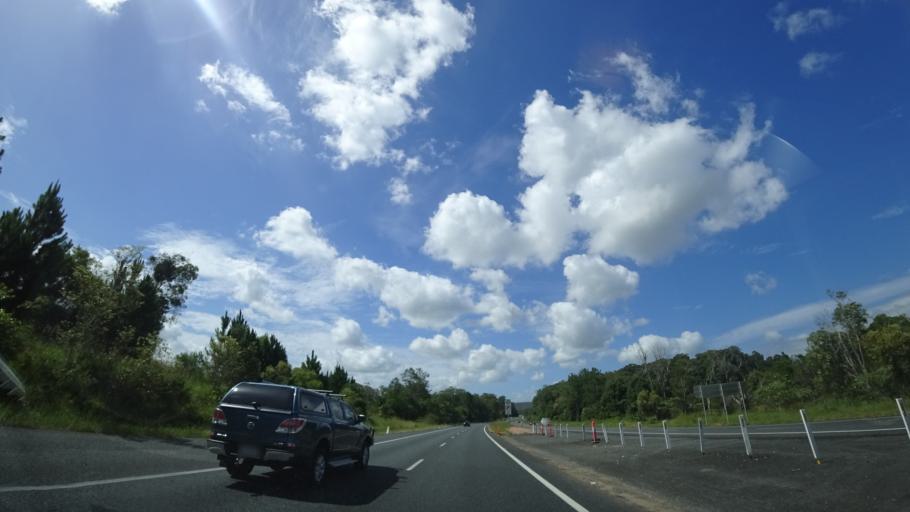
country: AU
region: Queensland
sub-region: Sunshine Coast
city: Woombye
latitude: -26.6406
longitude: 152.9873
